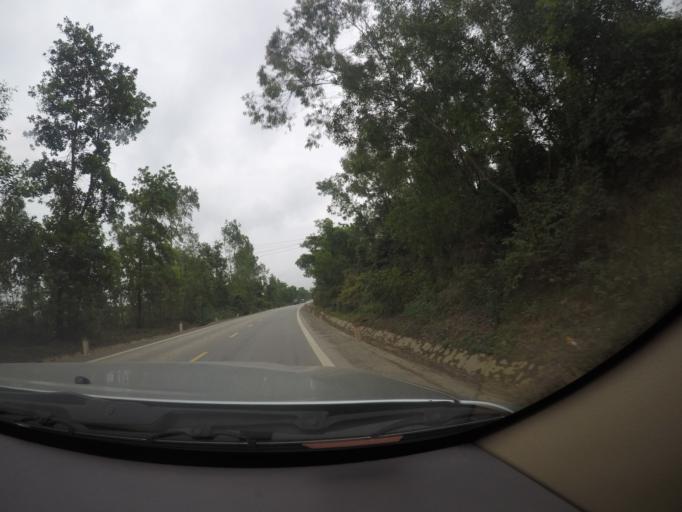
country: VN
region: Quang Binh
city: Quan Hau
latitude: 17.3092
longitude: 106.6381
